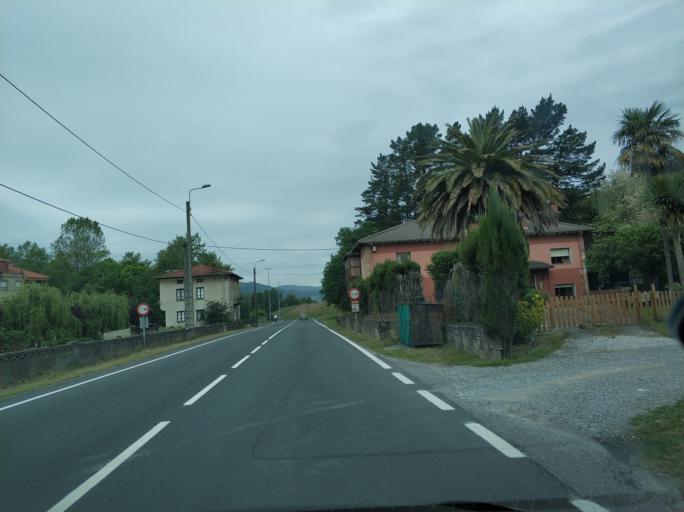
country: ES
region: Cantabria
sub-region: Provincia de Cantabria
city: Santa Maria de Cayon
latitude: 43.3230
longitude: -3.8588
